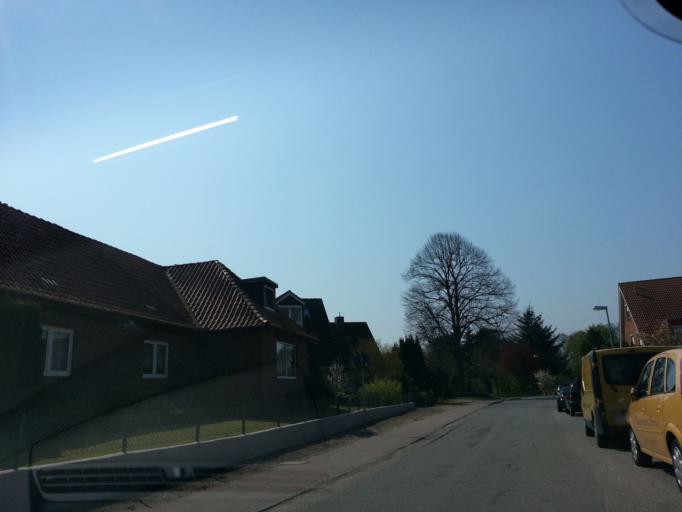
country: DE
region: Schleswig-Holstein
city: Ratekau
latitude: 53.9487
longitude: 10.7404
